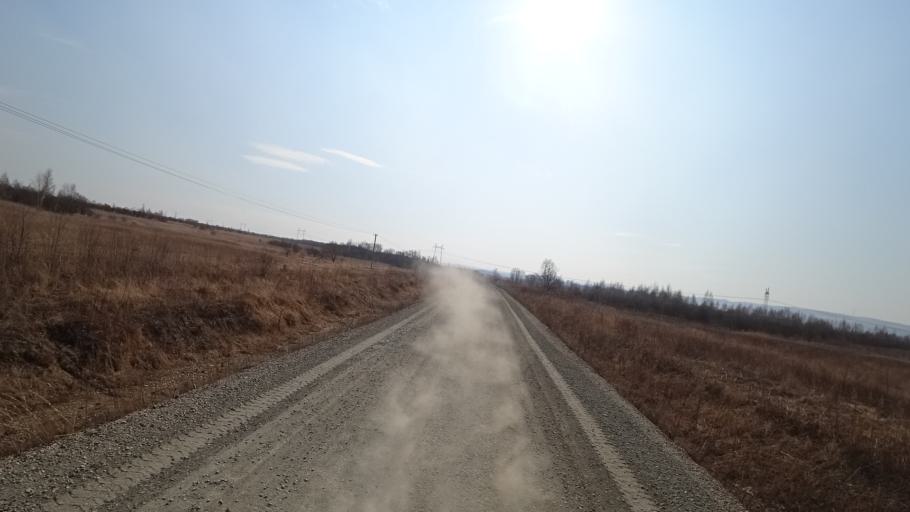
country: RU
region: Amur
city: Novobureyskiy
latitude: 49.8180
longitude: 129.9788
